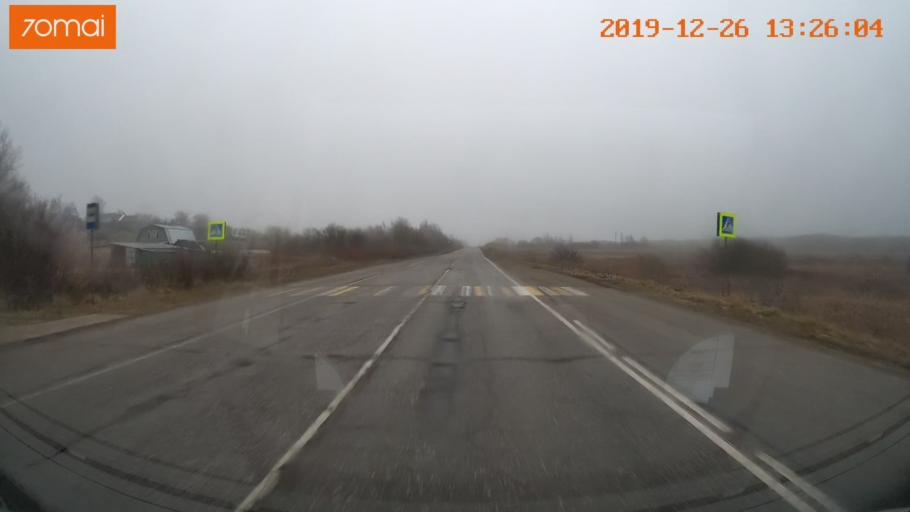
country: RU
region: Vologda
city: Cherepovets
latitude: 58.8685
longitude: 38.2198
